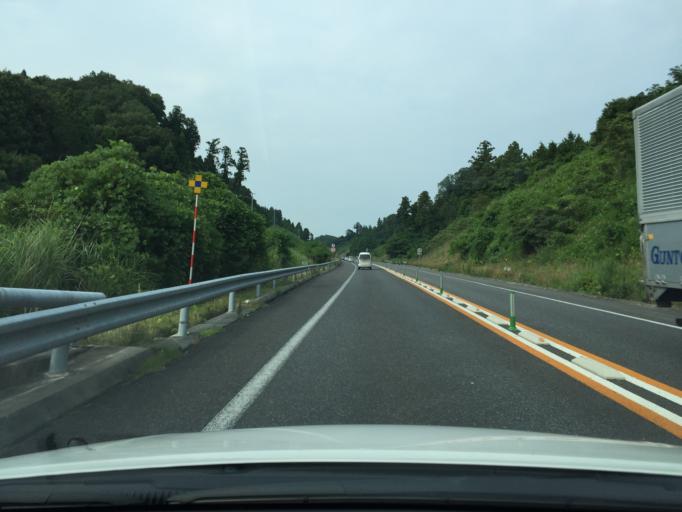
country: JP
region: Fukushima
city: Iwaki
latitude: 37.1823
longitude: 140.9812
